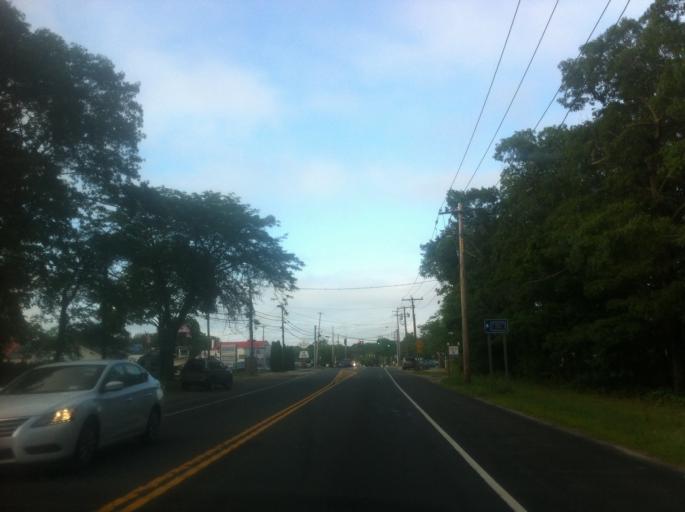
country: US
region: New York
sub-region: Suffolk County
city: Mattituck
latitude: 40.9784
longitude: -72.5459
